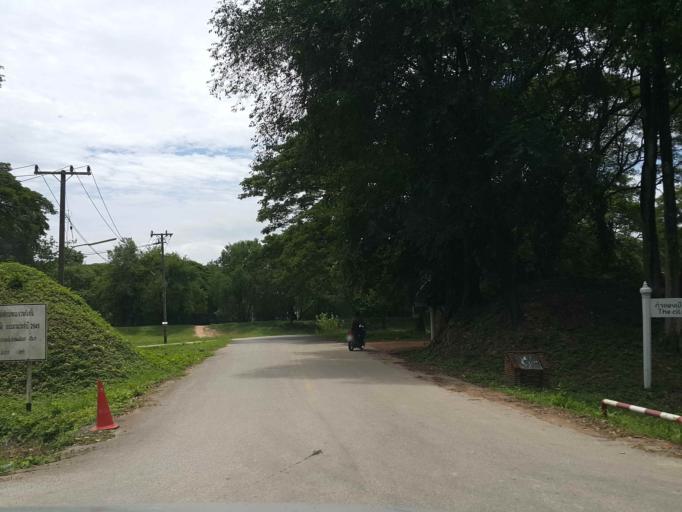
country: TH
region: Sukhothai
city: Ban Na
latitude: 17.0124
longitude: 99.7059
